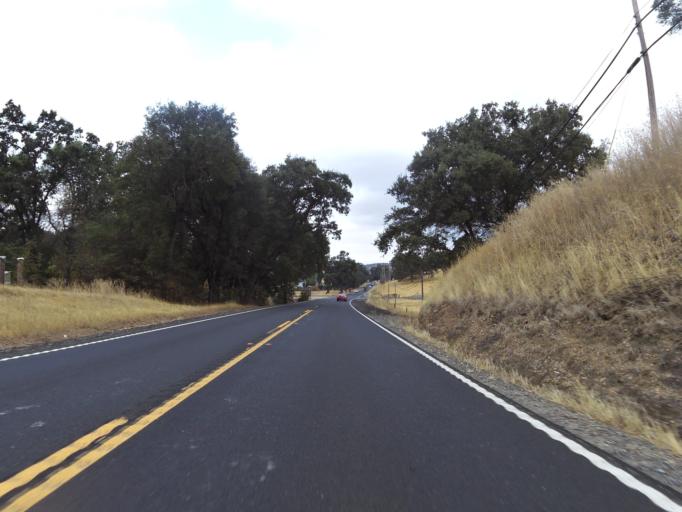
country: US
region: California
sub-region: Calaveras County
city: Angels Camp
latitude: 38.0989
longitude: -120.5878
